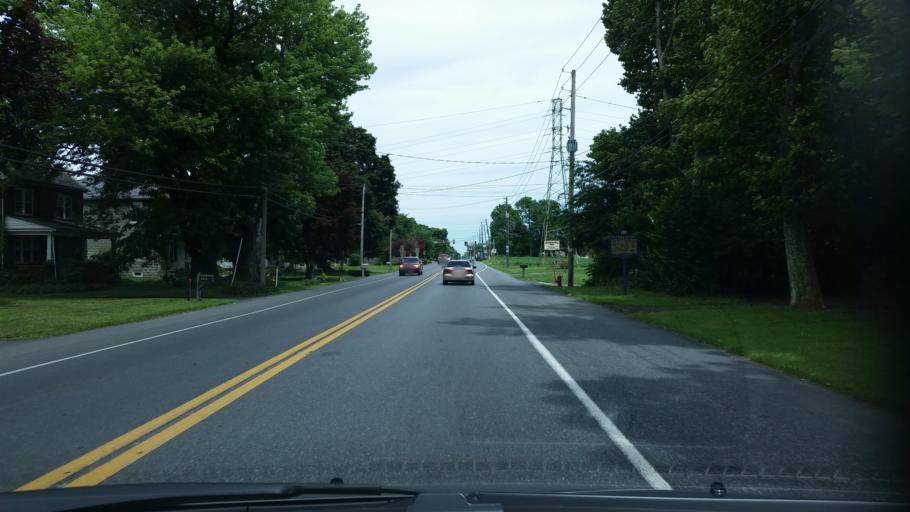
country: US
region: Pennsylvania
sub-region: Lancaster County
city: Lampeter
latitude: 40.0402
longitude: -76.2419
